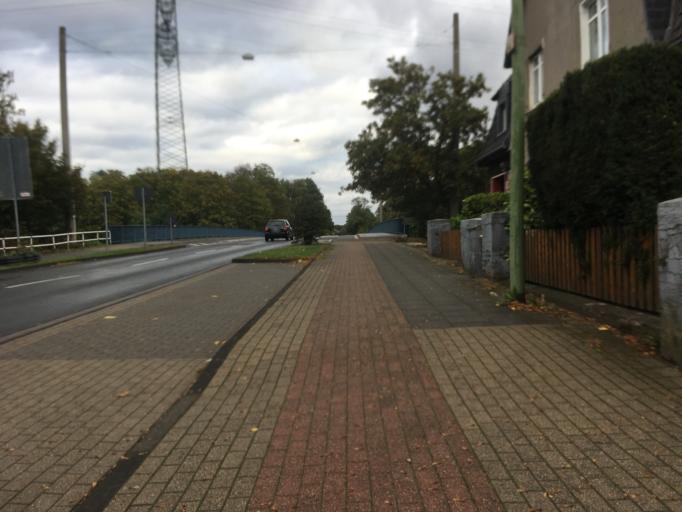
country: DE
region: North Rhine-Westphalia
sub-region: Regierungsbezirk Munster
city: Bottrop
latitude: 51.4972
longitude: 6.9353
